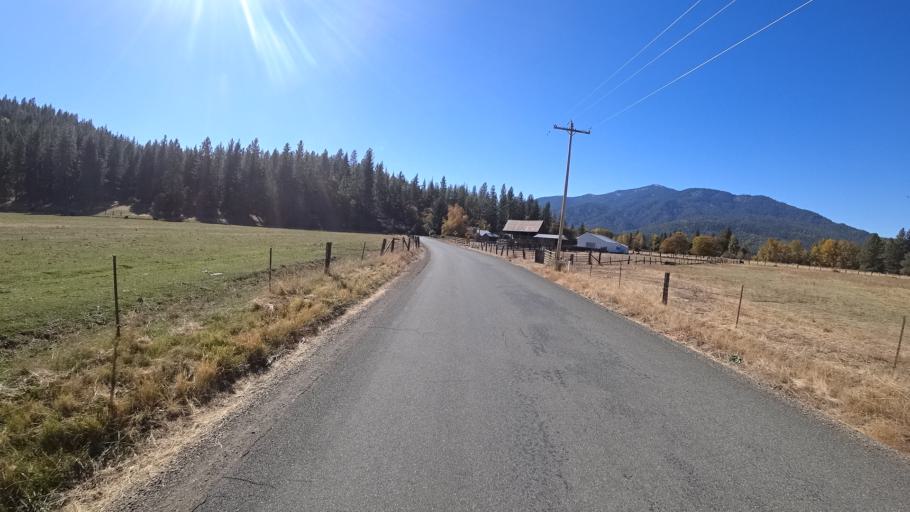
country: US
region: California
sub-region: Siskiyou County
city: Yreka
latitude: 41.6261
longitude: -122.9605
